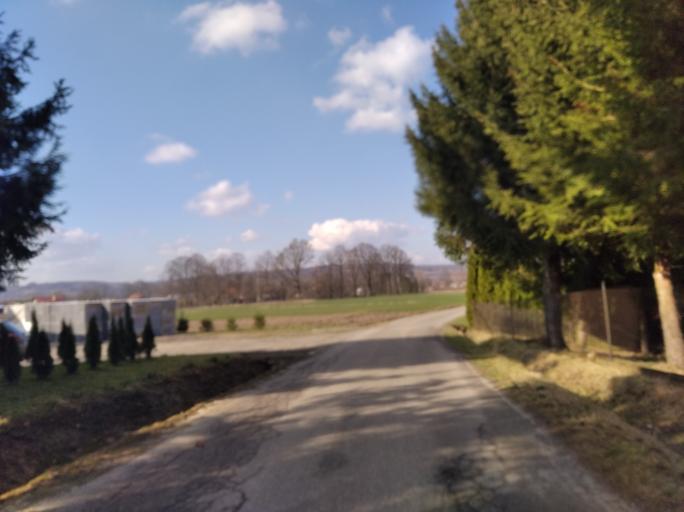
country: PL
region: Subcarpathian Voivodeship
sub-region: Powiat strzyzowski
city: Wysoka Strzyzowska
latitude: 49.8560
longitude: 21.7091
